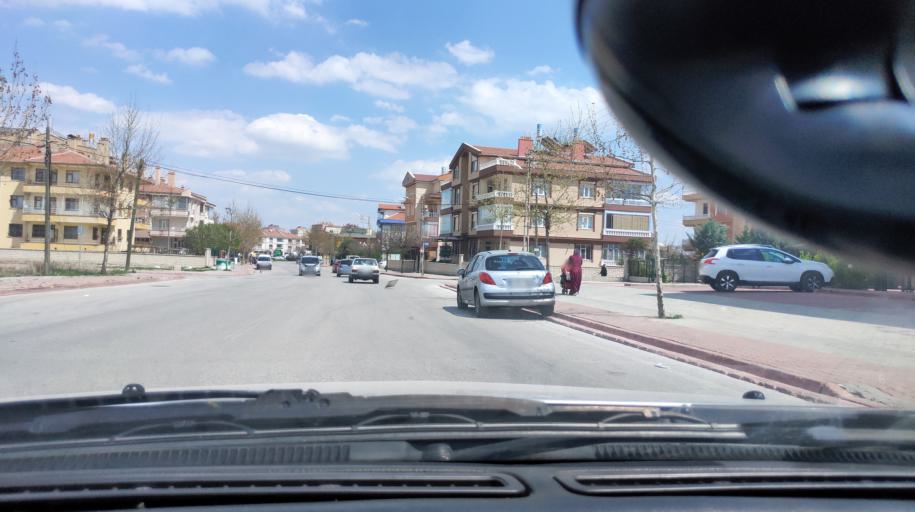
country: TR
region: Konya
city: Selcuklu
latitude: 37.9293
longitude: 32.4908
